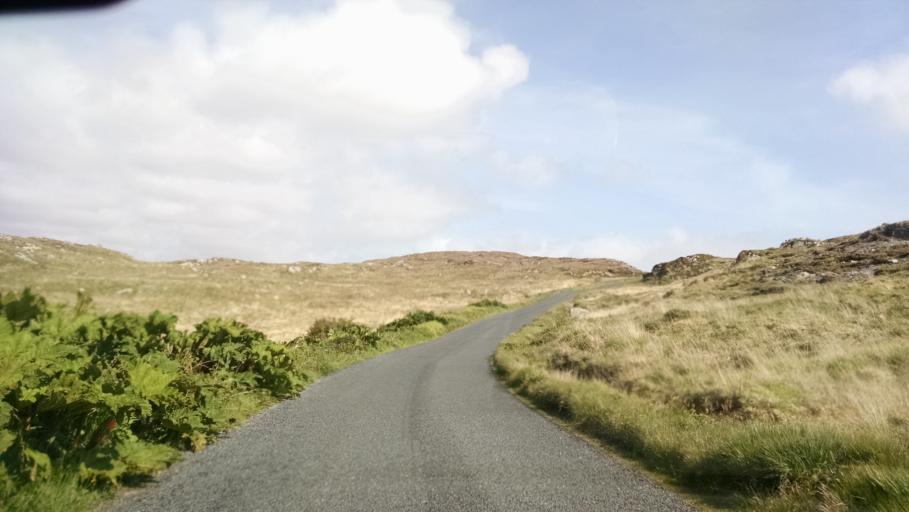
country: IE
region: Connaught
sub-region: County Galway
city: Clifden
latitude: 53.5046
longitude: -10.1047
